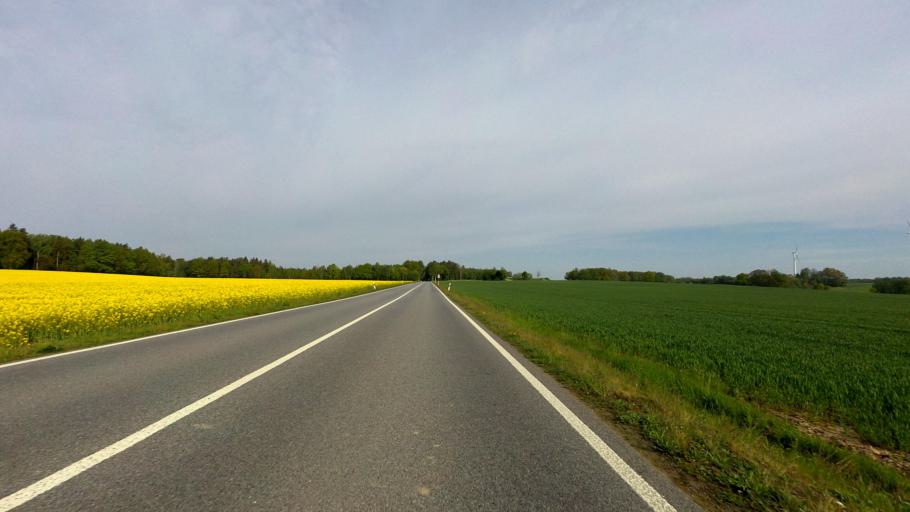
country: DE
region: Saxony
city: Stolpen
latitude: 51.0672
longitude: 14.0500
